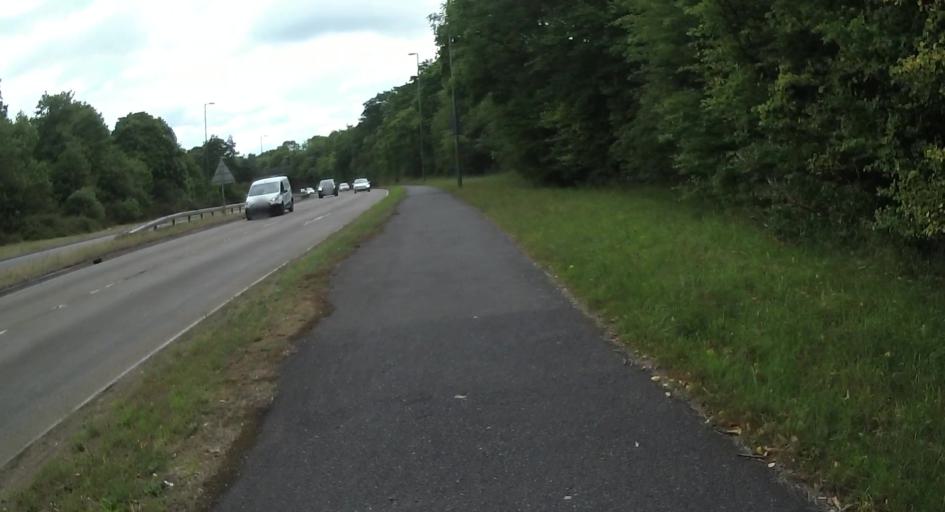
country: GB
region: England
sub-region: Surrey
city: Farnham
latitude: 51.2085
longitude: -0.7989
